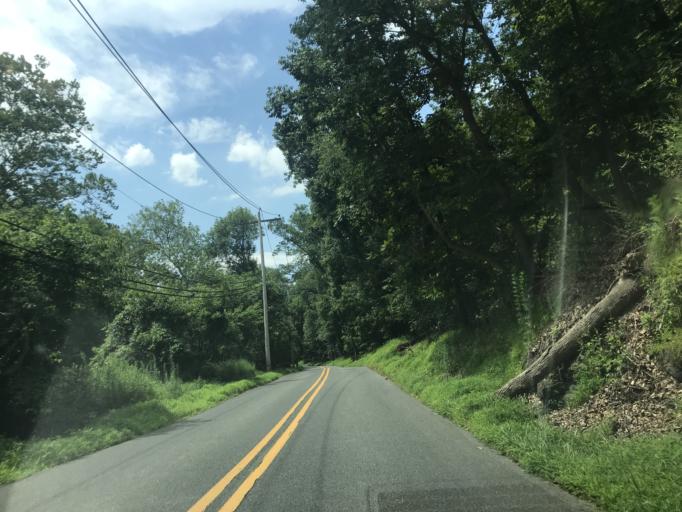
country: US
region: Delaware
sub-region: New Castle County
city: Greenville
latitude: 39.7716
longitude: -75.6374
